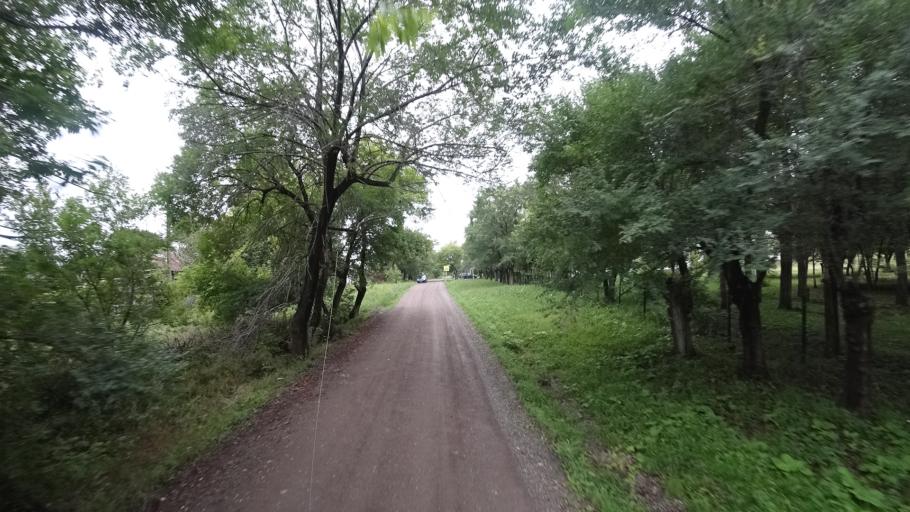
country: RU
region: Primorskiy
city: Chernigovka
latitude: 44.3395
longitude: 132.5455
